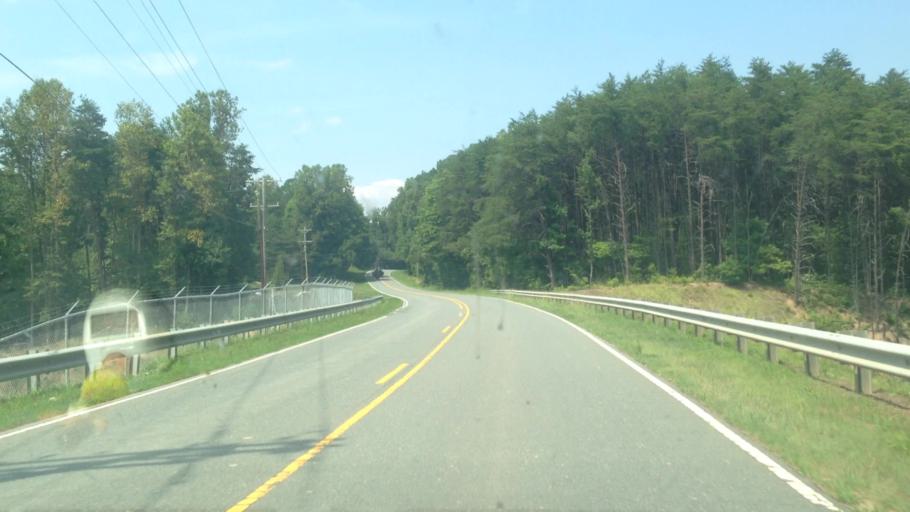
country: US
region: North Carolina
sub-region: Stokes County
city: Walnut Cove
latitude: 36.2958
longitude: -80.0622
